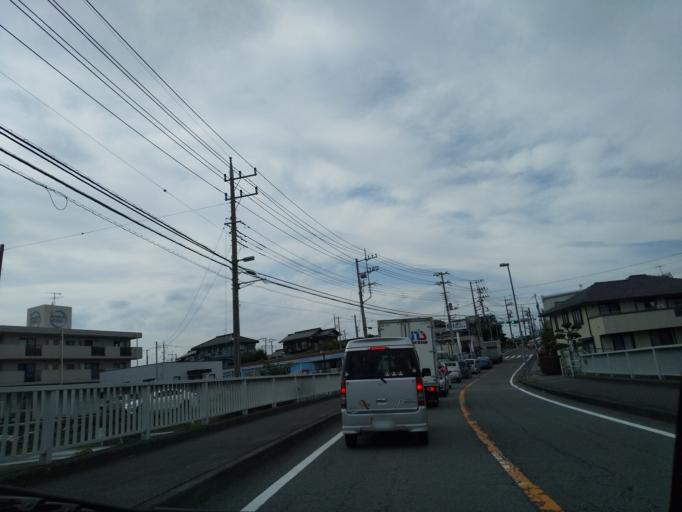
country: JP
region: Kanagawa
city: Atsugi
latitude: 35.4745
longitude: 139.3406
